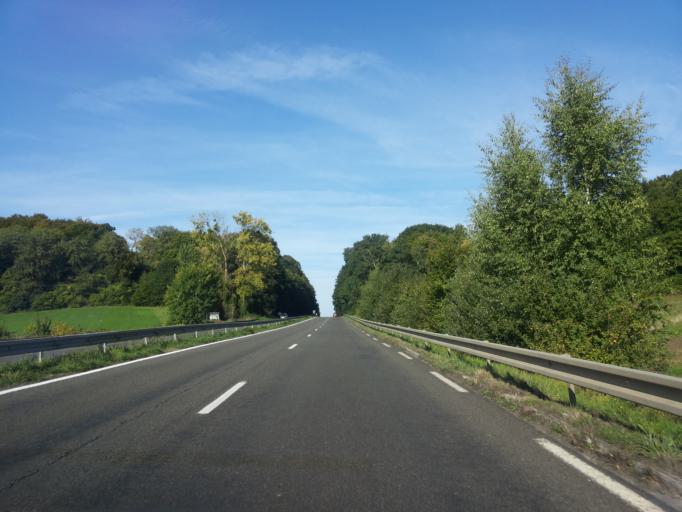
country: FR
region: Picardie
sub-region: Departement de l'Aisne
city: Crepy
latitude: 49.6096
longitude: 3.4964
